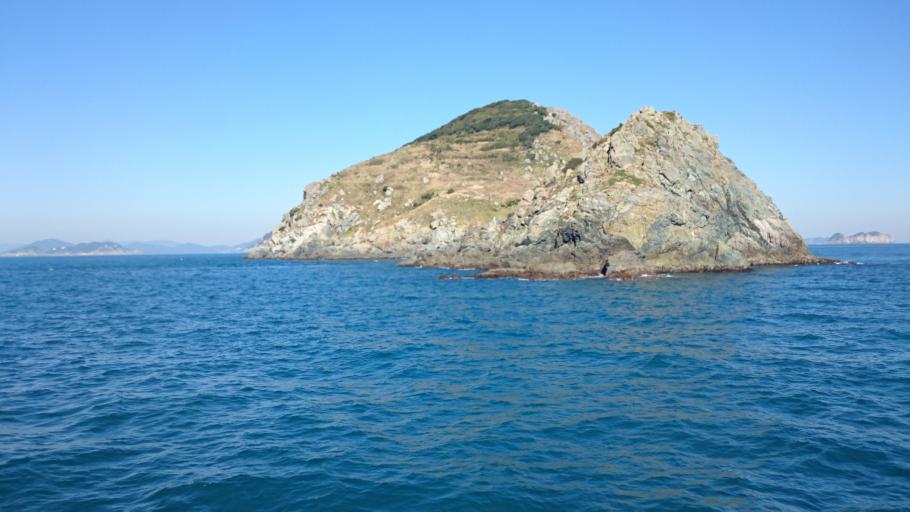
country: KR
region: Gyeongsangnam-do
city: Kyosai
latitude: 34.6508
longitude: 128.5719
